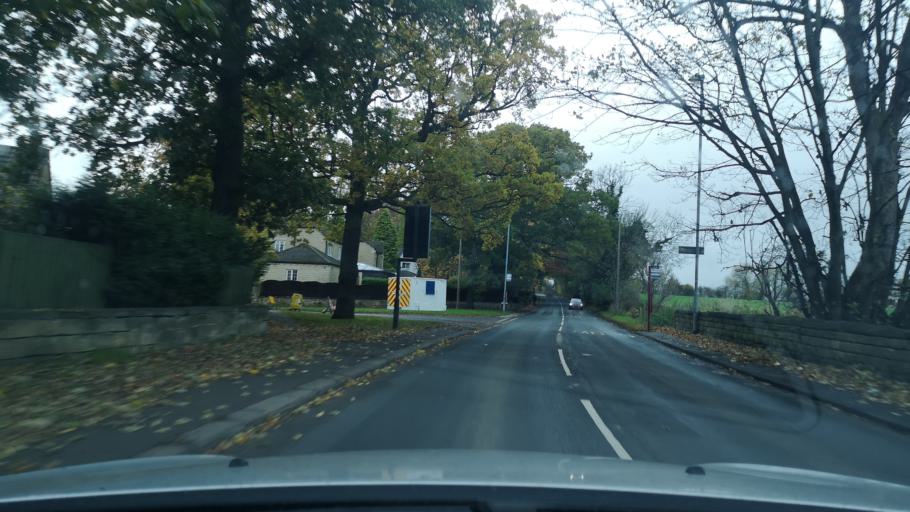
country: GB
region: England
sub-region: City and Borough of Wakefield
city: Low Ackworth
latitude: 53.6582
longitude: -1.3296
